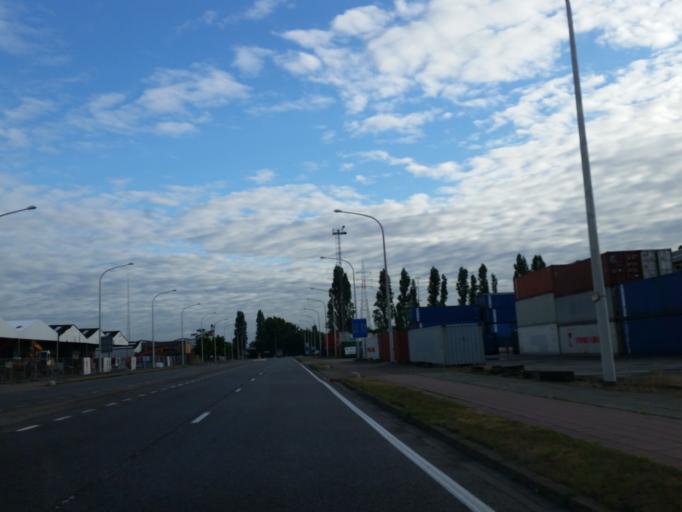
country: BE
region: Flanders
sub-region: Provincie Antwerpen
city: Antwerpen
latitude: 51.2698
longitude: 4.4007
